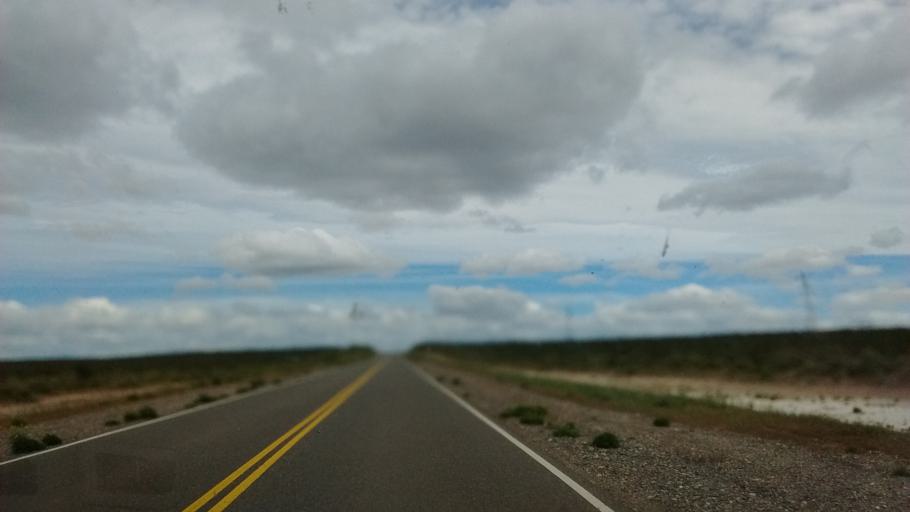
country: AR
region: Neuquen
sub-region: Departamento de Picun Leufu
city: Picun Leufu
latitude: -39.6595
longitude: -69.4214
